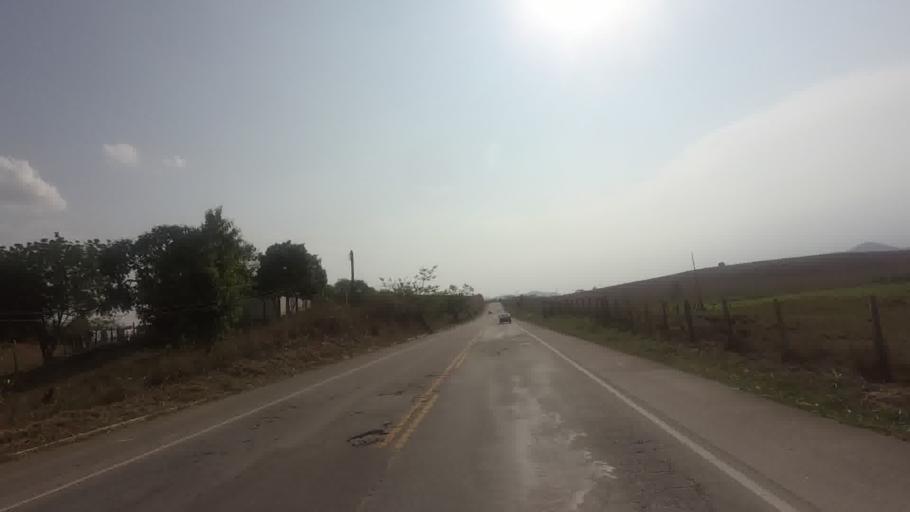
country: BR
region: Rio de Janeiro
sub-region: Bom Jesus Do Itabapoana
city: Bom Jesus do Itabapoana
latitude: -21.1529
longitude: -41.6048
